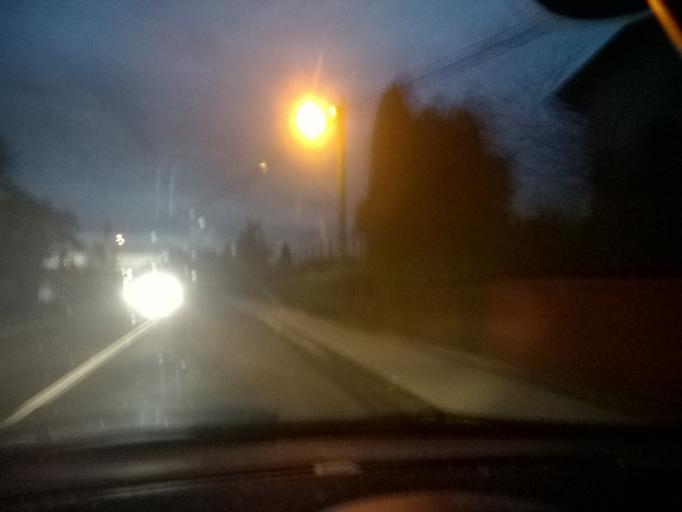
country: HR
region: Krapinsko-Zagorska
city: Zabok
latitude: 46.0357
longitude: 15.9290
